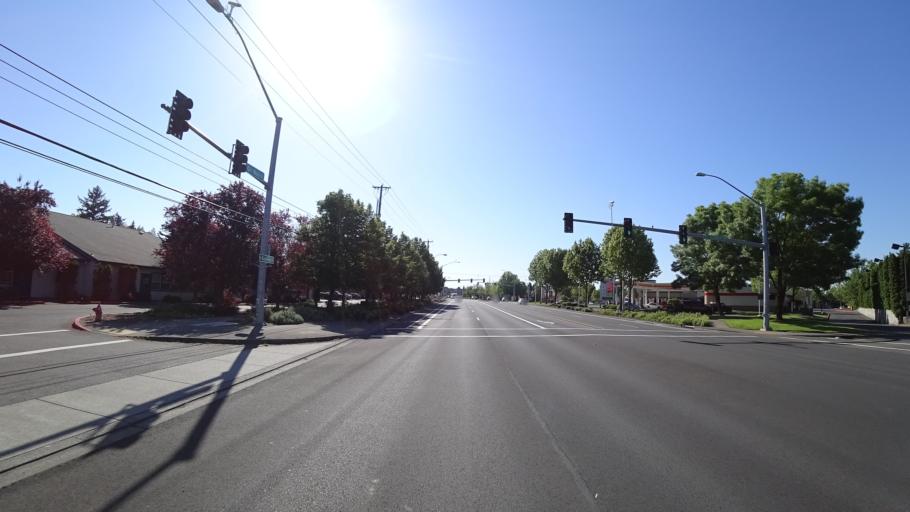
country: US
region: Oregon
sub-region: Washington County
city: Rockcreek
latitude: 45.5166
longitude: -122.9045
